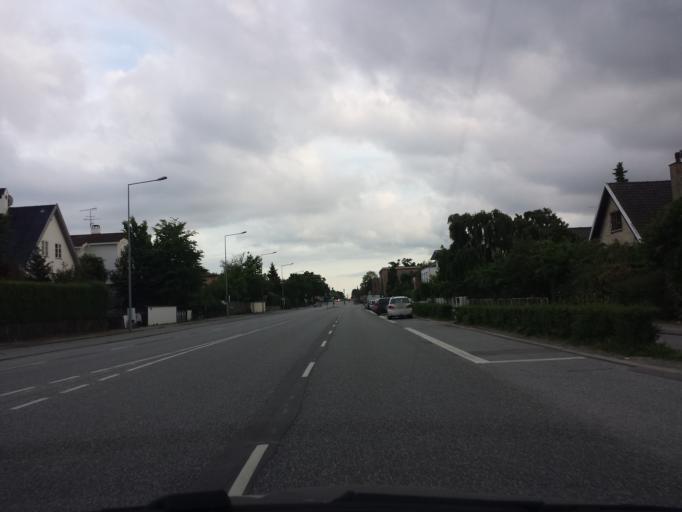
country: DK
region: Capital Region
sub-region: Gentofte Kommune
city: Charlottenlund
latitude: 55.7519
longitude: 12.5577
